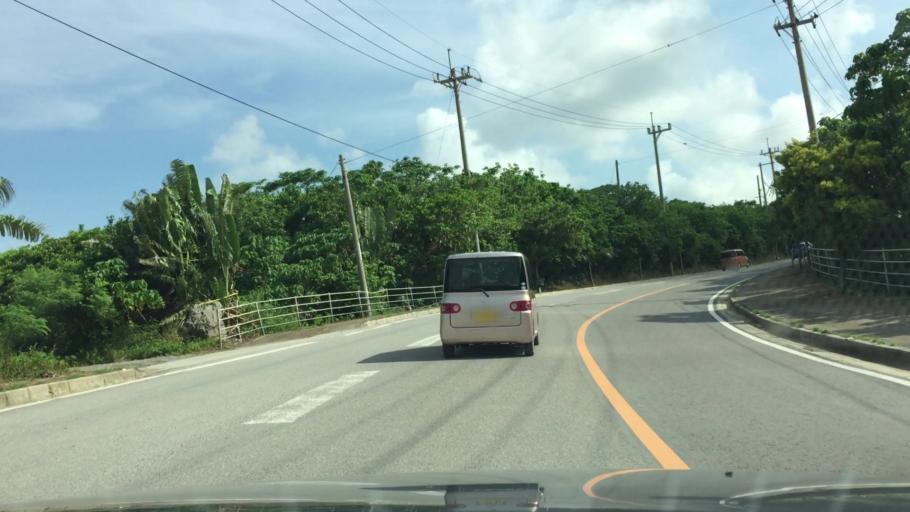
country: JP
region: Okinawa
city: Ishigaki
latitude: 24.4301
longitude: 124.2477
